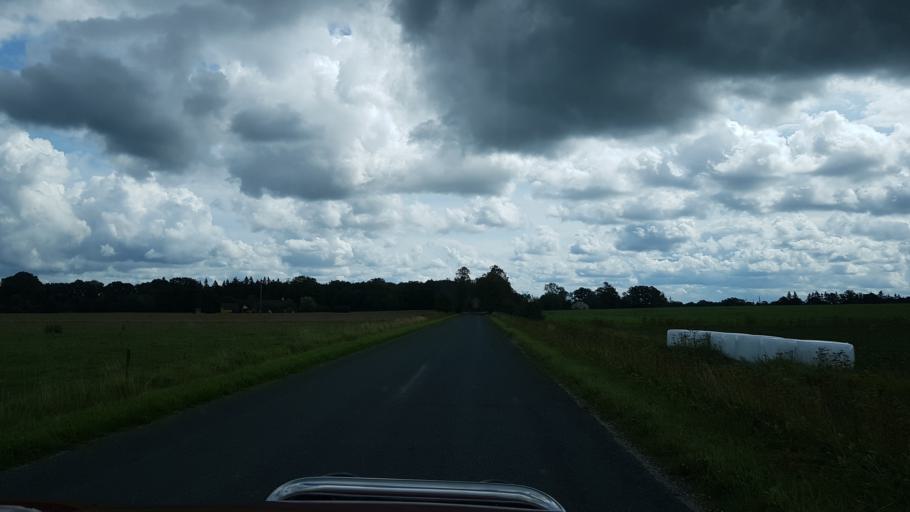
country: EE
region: Laeaene
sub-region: Lihula vald
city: Lihula
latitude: 58.7092
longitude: 24.0167
